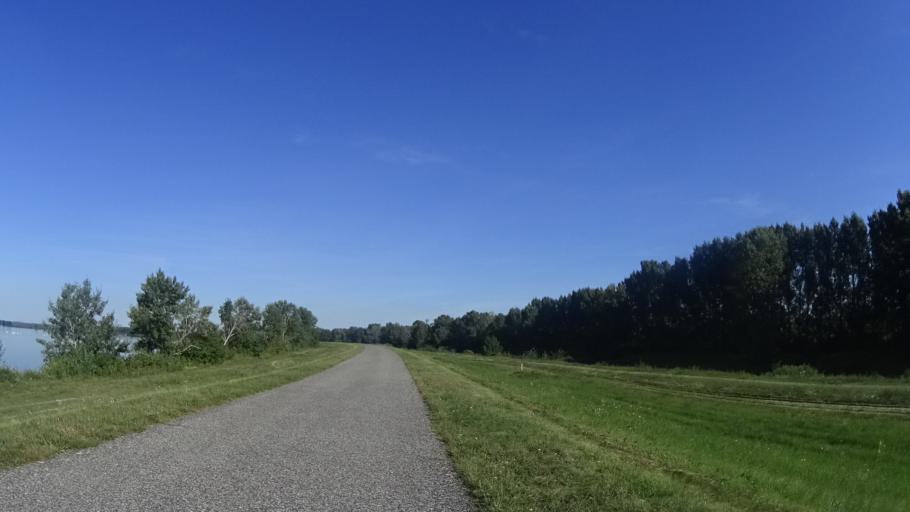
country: SK
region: Bratislavsky
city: Dunajska Luzna
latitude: 48.0518
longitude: 17.2357
